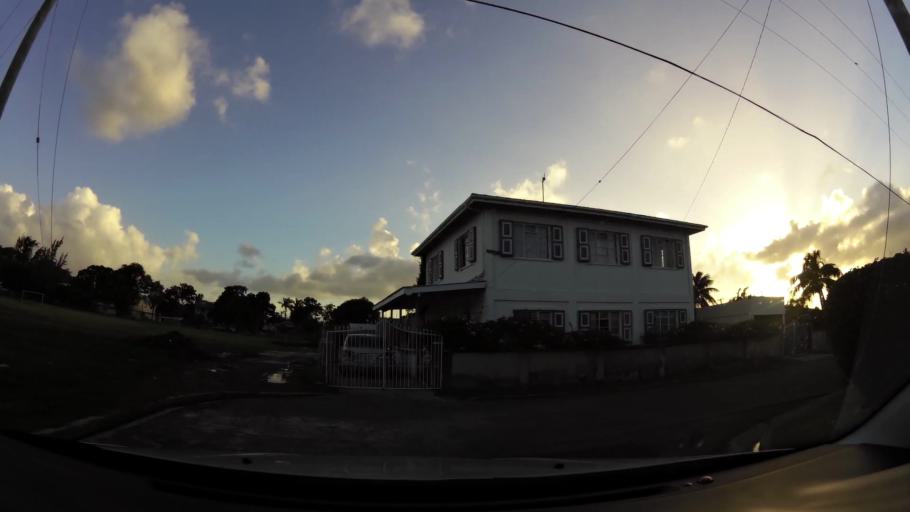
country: AG
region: Saint John
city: Saint John's
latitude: 17.1269
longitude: -61.8441
